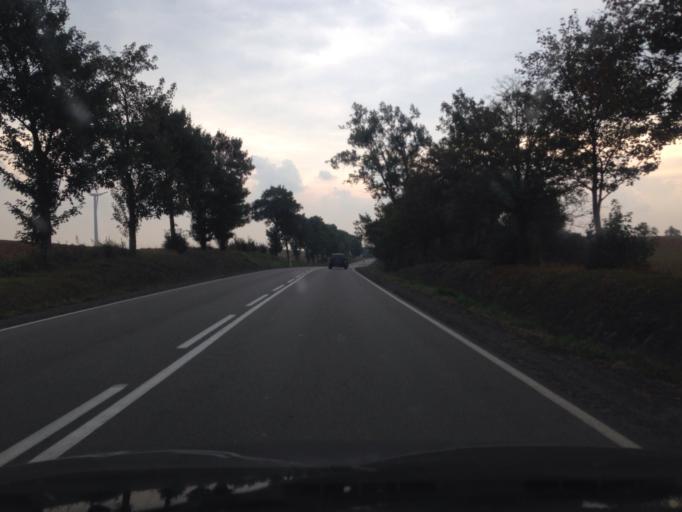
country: PL
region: Pomeranian Voivodeship
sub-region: Powiat sztumski
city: Sztum
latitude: 53.9700
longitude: 19.0105
